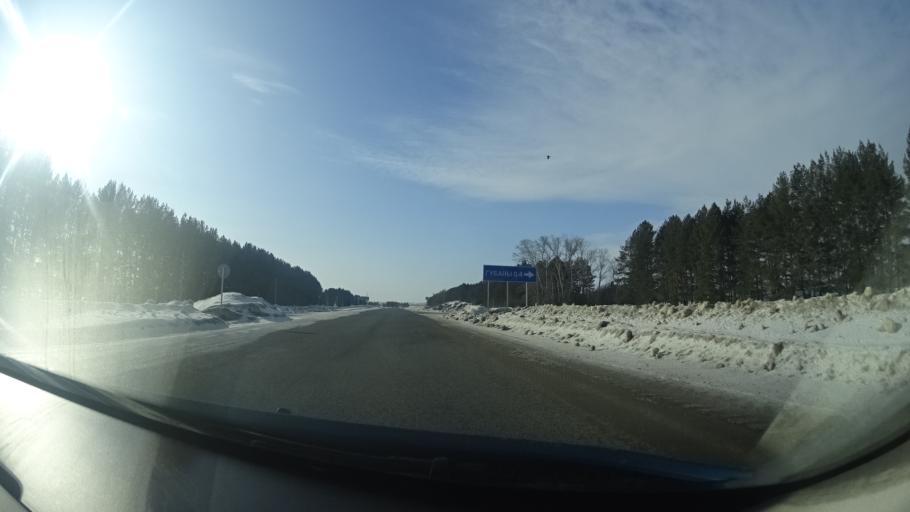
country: RU
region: Perm
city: Kuyeda
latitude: 56.4794
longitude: 55.5909
